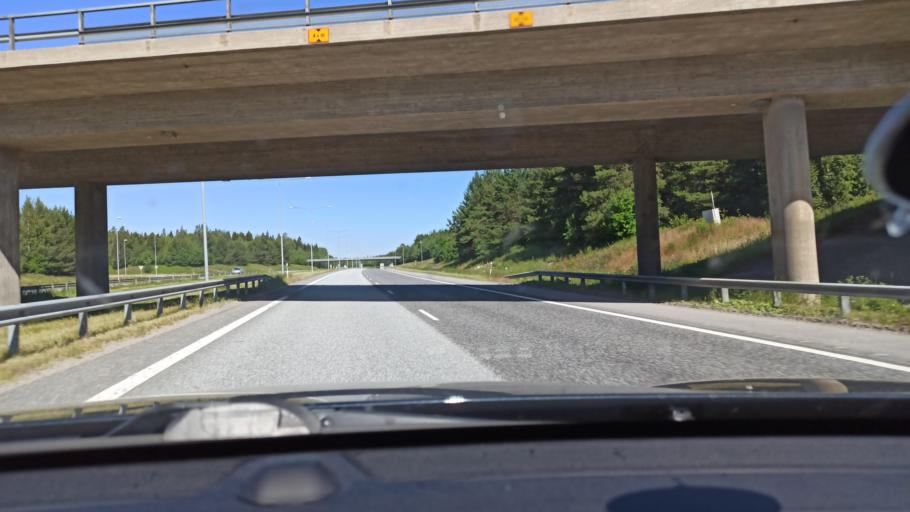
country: FI
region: Ostrobothnia
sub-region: Vaasa
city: Ristinummi
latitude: 63.0531
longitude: 21.7151
